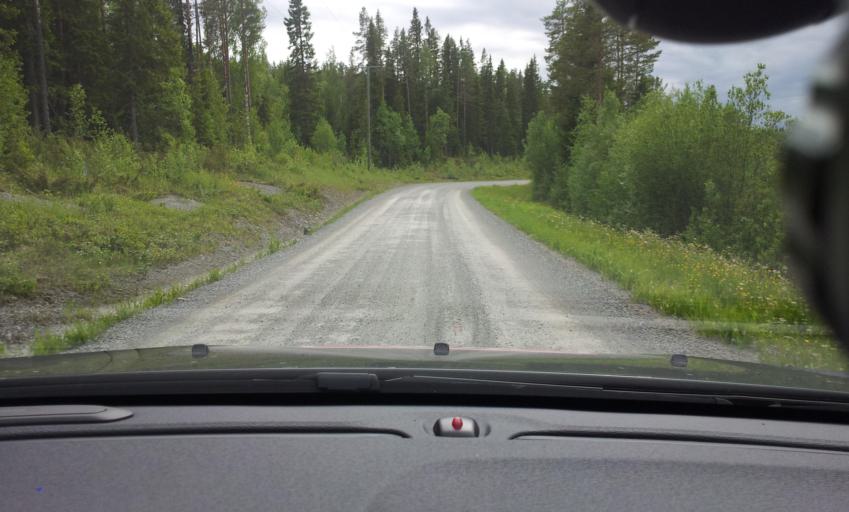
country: SE
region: Jaemtland
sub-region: OEstersunds Kommun
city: Brunflo
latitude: 62.9938
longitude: 14.7325
